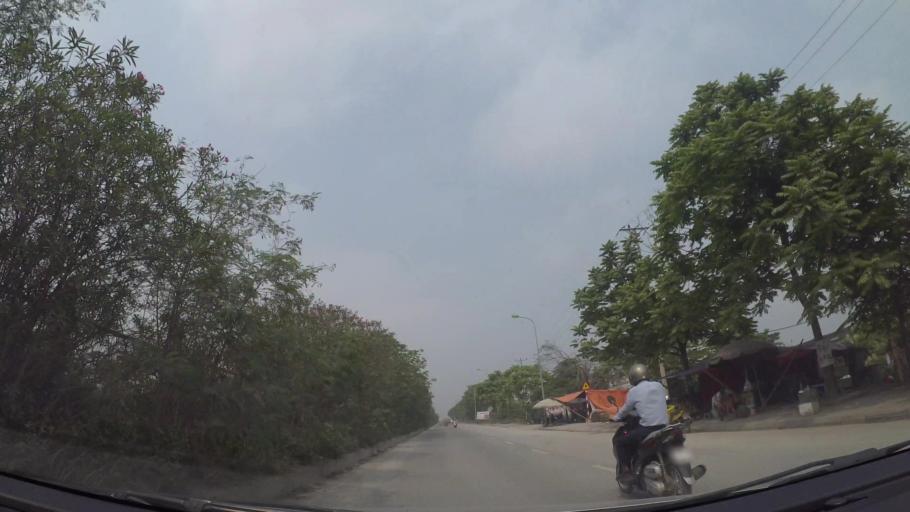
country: VN
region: Ha Noi
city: Troi
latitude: 21.0087
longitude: 105.7030
